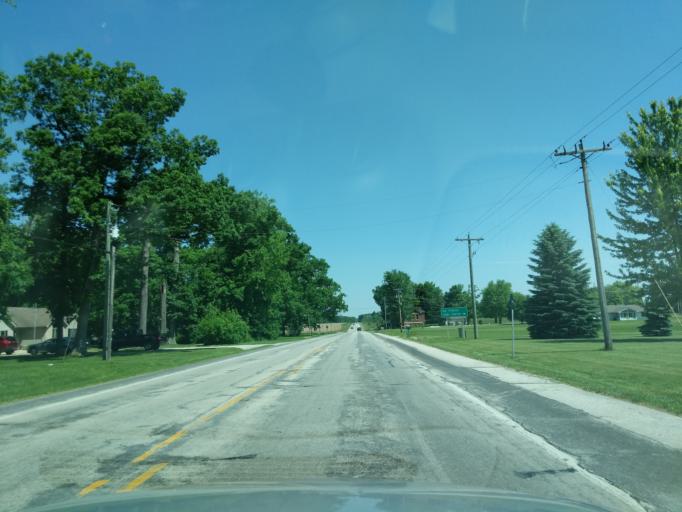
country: US
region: Indiana
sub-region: Whitley County
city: Columbia City
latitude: 41.1019
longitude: -85.4714
